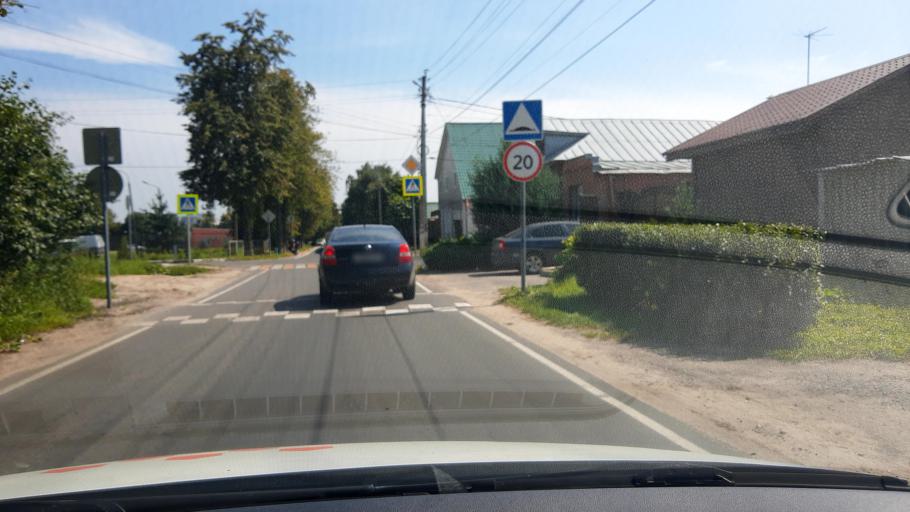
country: RU
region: Moskovskaya
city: Bronnitsy
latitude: 55.4218
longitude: 38.2653
